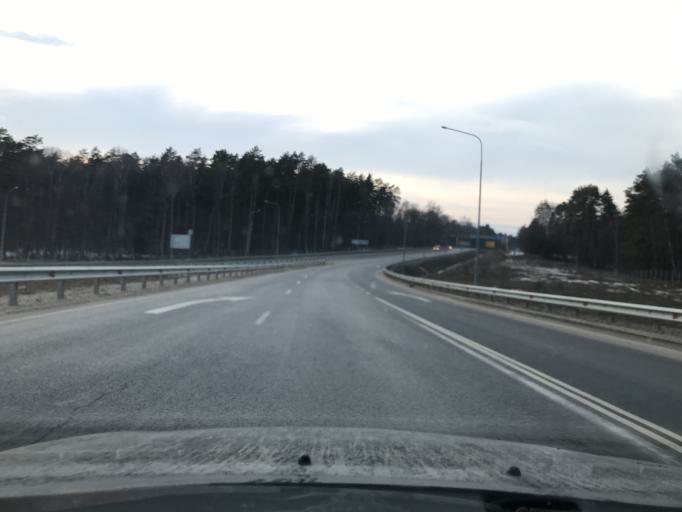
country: RU
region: Kaluga
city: Mstikhino
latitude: 54.5871
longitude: 36.0708
